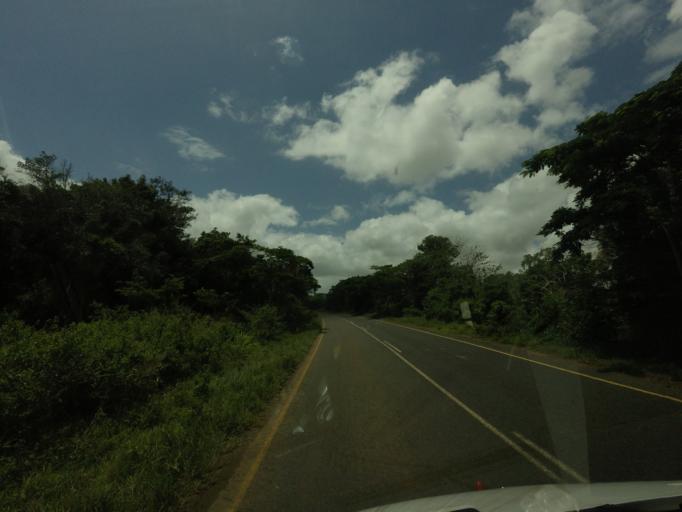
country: ZA
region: KwaZulu-Natal
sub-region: uMkhanyakude District Municipality
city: Mtubatuba
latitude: -28.3888
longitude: 32.3355
